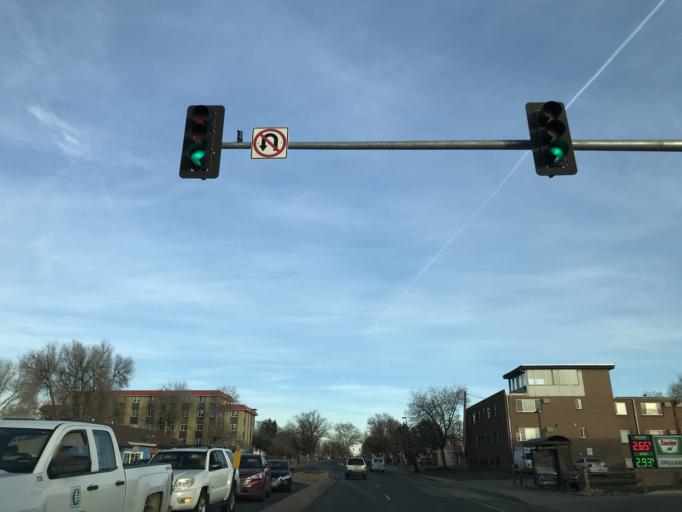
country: US
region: Colorado
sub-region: Adams County
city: Aurora
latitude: 39.7474
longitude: -104.8753
